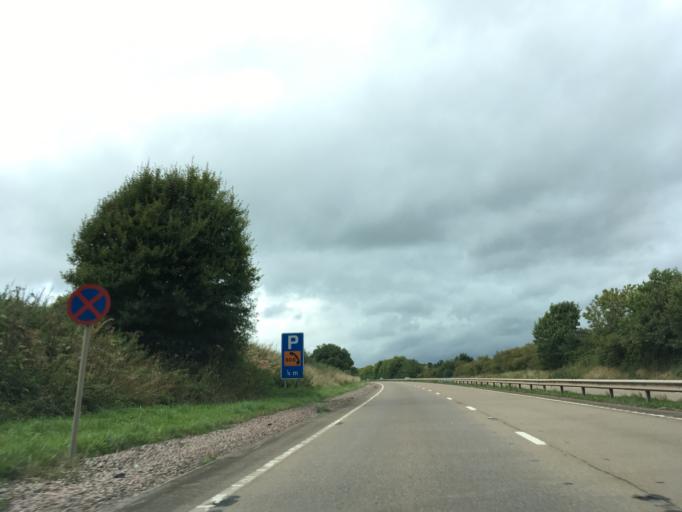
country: GB
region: Wales
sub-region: Monmouthshire
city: Llanarth
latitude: 51.7737
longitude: -2.8745
